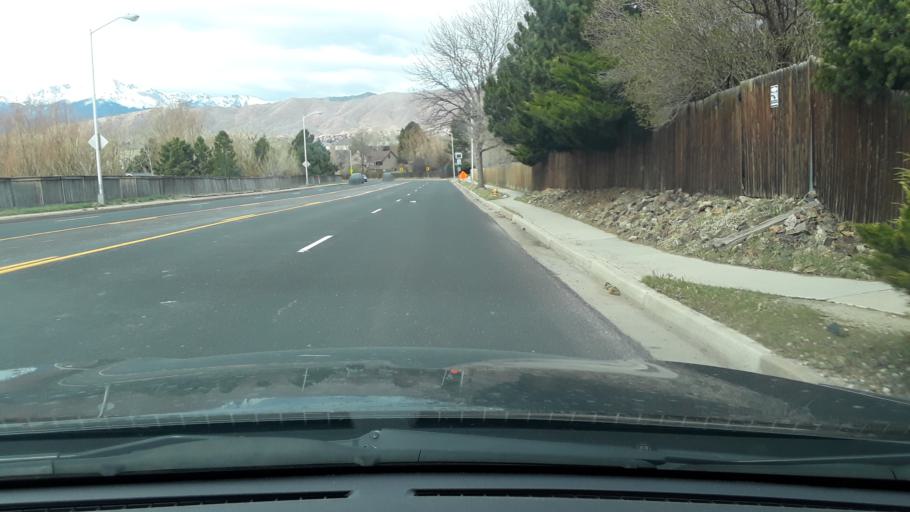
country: US
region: Colorado
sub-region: El Paso County
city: Air Force Academy
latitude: 38.9258
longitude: -104.8386
